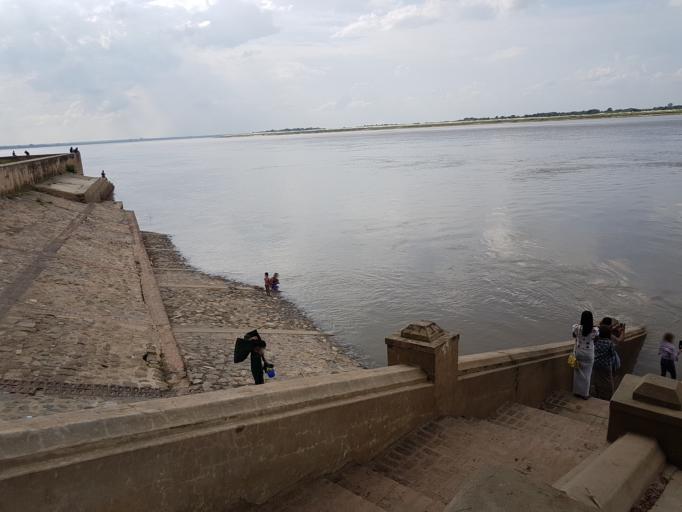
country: MM
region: Sagain
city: Sagaing
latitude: 21.8564
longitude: 95.9597
